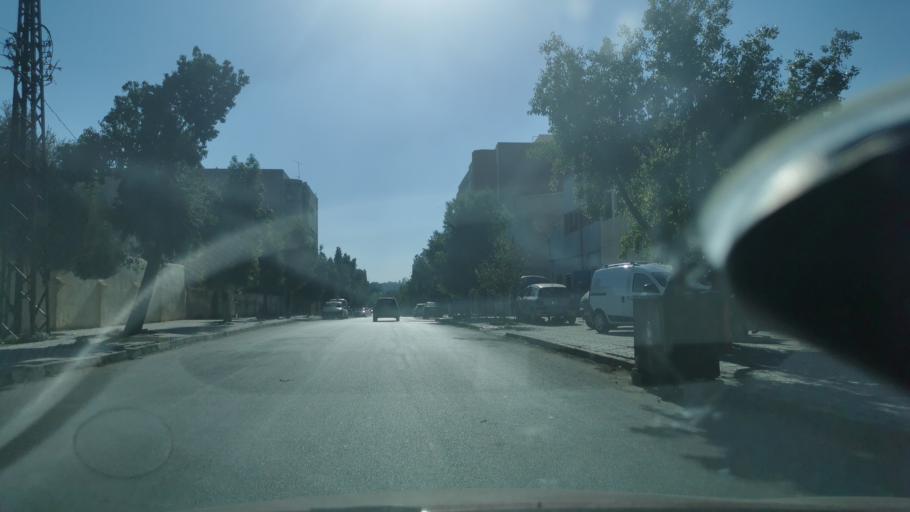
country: MA
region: Fes-Boulemane
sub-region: Fes
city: Fes
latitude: 34.0357
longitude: -4.9905
